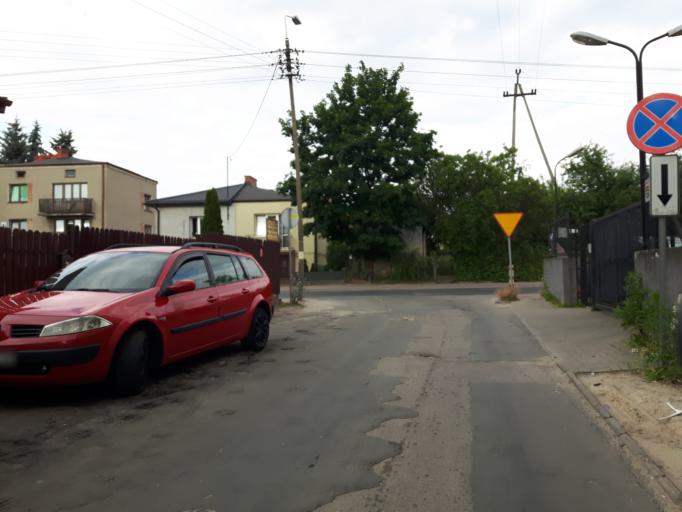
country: PL
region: Masovian Voivodeship
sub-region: Powiat wolominski
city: Zabki
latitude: 52.2829
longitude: 21.1104
